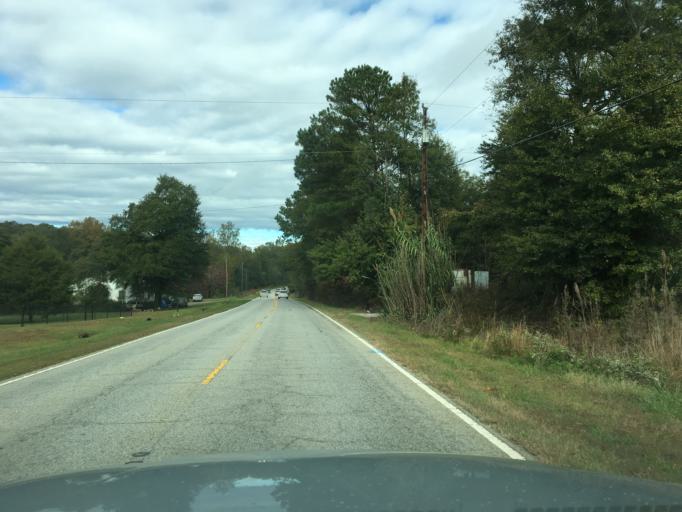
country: US
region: South Carolina
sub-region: Greenville County
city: Greer
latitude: 35.0153
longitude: -82.2620
